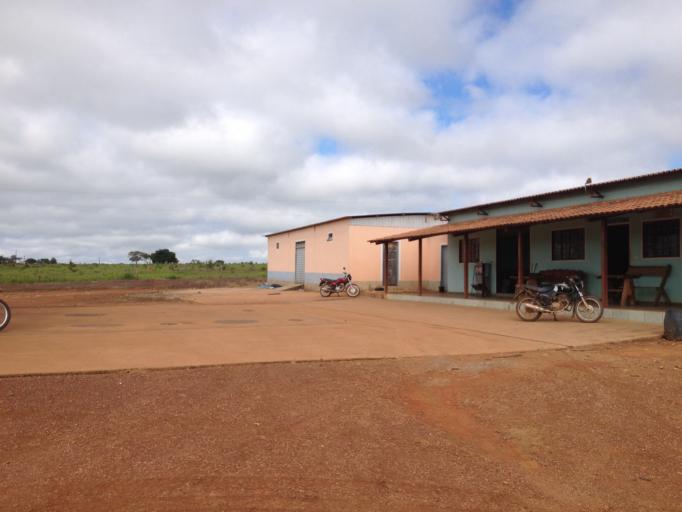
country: BR
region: Goias
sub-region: Orizona
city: Orizona
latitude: -16.9538
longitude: -48.0086
